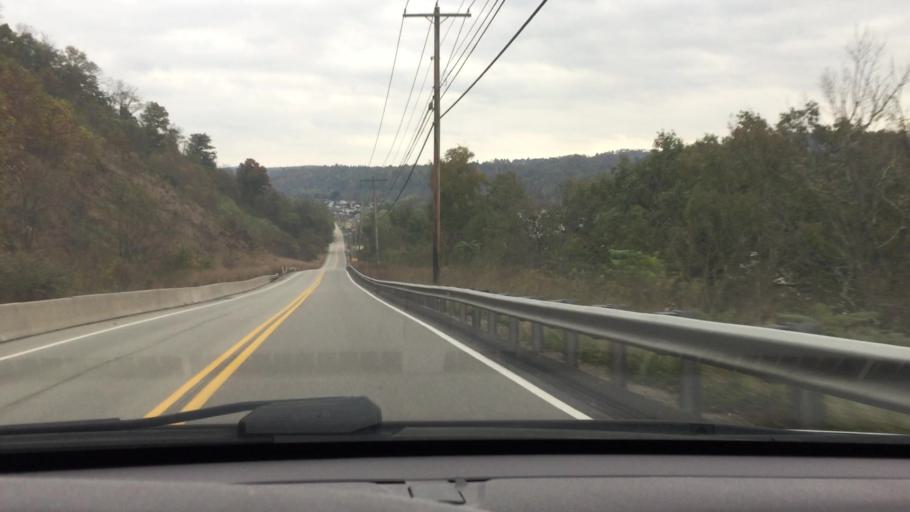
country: US
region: Pennsylvania
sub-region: Washington County
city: California
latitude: 40.0816
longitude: -79.8849
